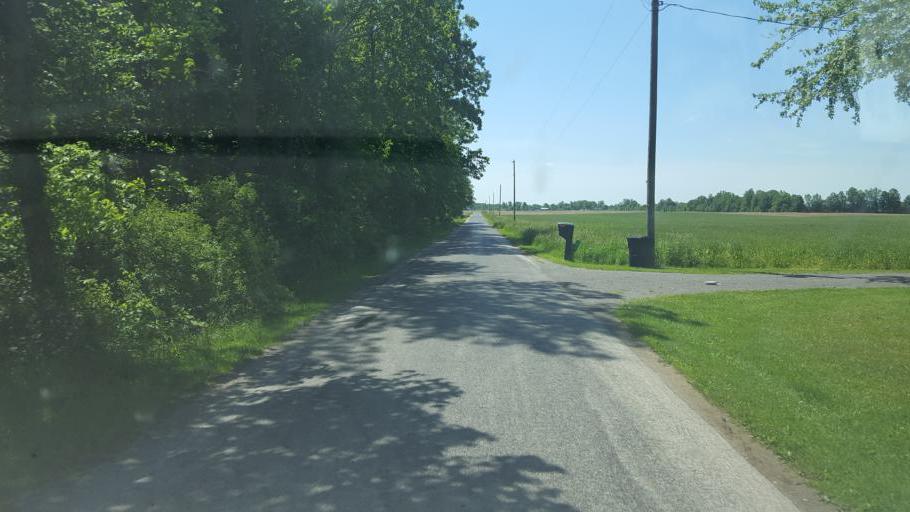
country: US
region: Ohio
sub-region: Union County
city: Richwood
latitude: 40.5836
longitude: -83.4087
